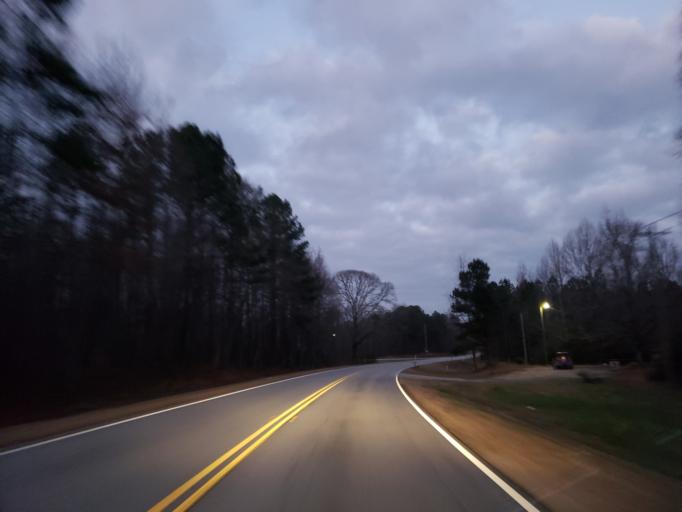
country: US
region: Georgia
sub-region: Carroll County
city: Temple
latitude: 33.7971
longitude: -85.0604
